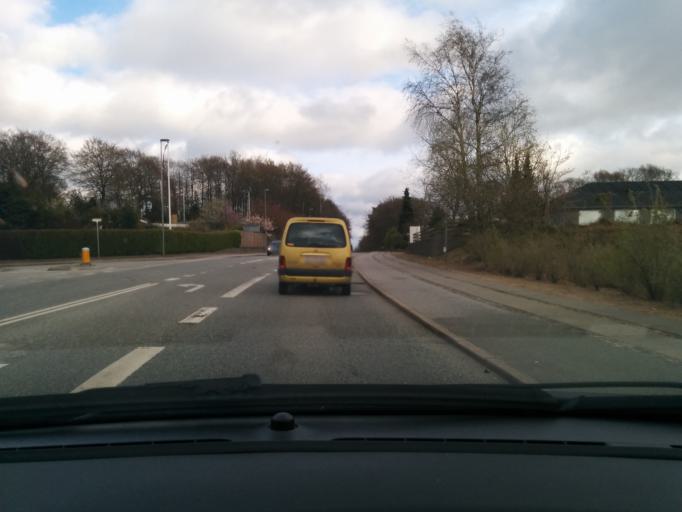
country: DK
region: Central Jutland
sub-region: Favrskov Kommune
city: Hadsten
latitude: 56.3262
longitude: 10.0593
